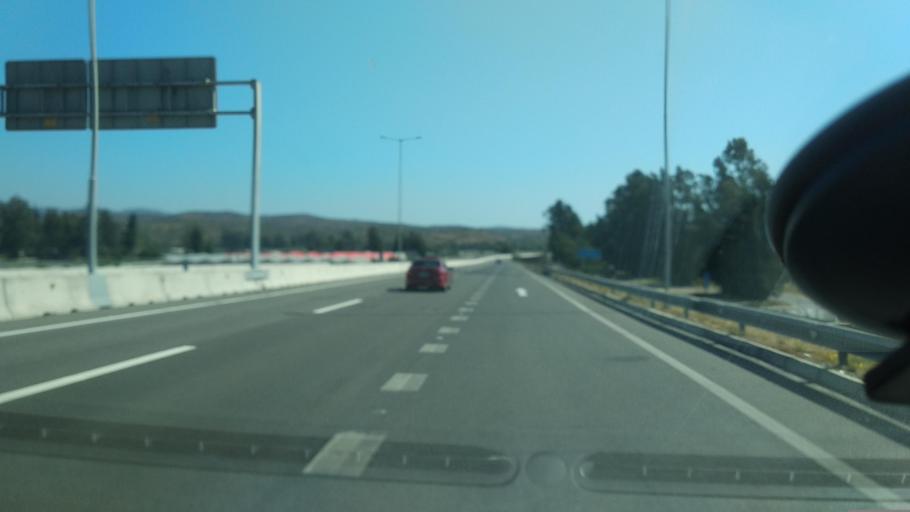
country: CL
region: Valparaiso
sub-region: Provincia de Marga Marga
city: Limache
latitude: -32.9743
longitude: -71.3034
